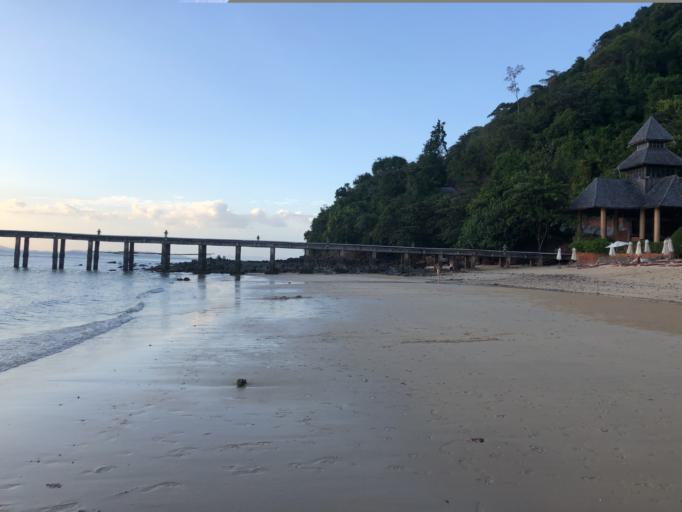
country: TH
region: Phangnga
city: Ban Phru Nai
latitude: 7.9821
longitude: 98.5682
